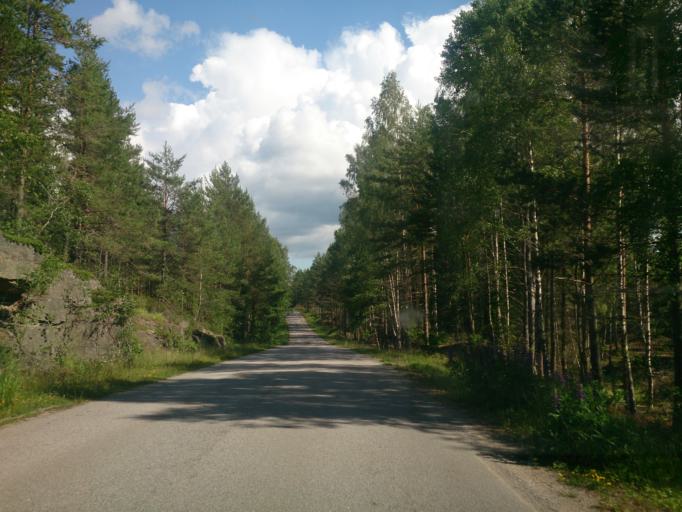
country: SE
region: OEstergoetland
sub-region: Norrkopings Kommun
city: Jursla
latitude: 58.7262
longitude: 16.1180
